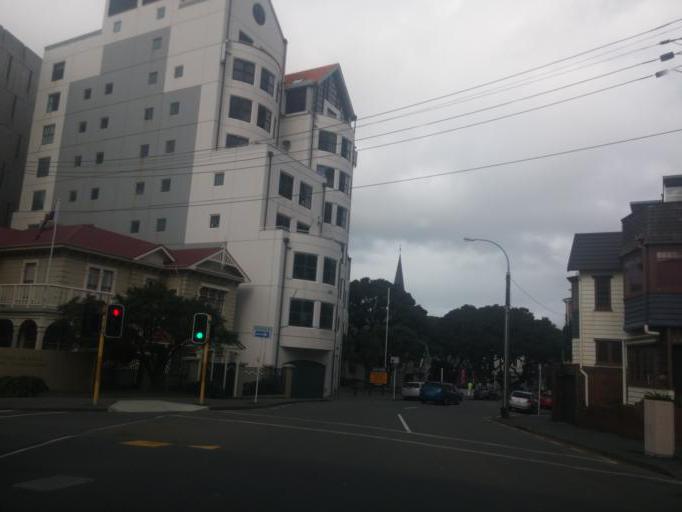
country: NZ
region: Wellington
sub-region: Wellington City
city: Wellington
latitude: -41.2755
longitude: 174.7798
